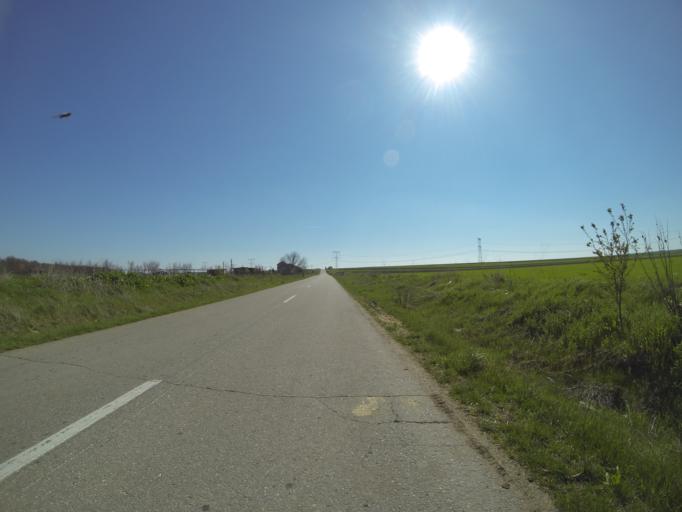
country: RO
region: Dolj
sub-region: Comuna Radovanu
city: Radovanu
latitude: 44.1516
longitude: 23.6016
